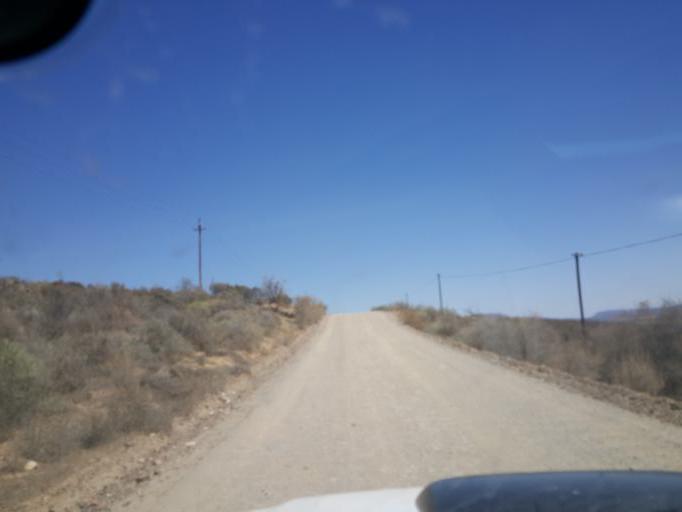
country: ZA
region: Western Cape
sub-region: West Coast District Municipality
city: Clanwilliam
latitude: -32.2089
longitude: 18.9031
